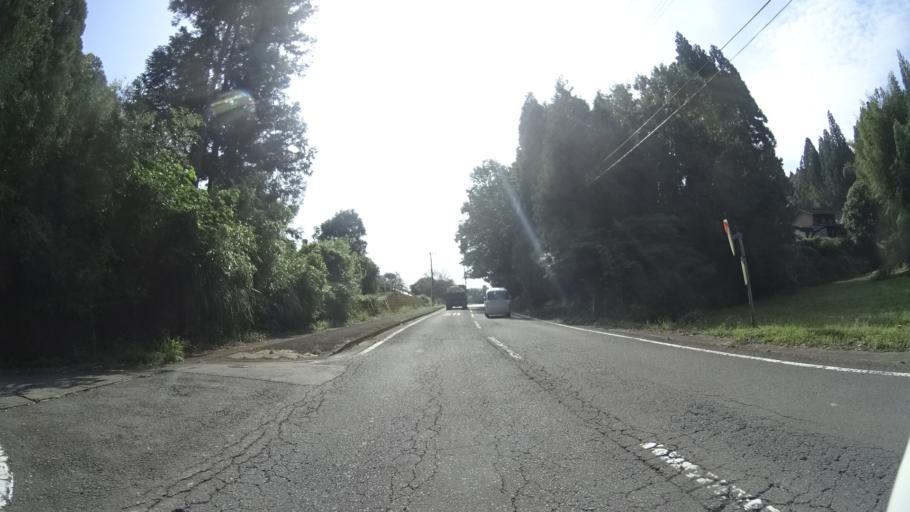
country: JP
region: Miyazaki
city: Kobayashi
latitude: 32.0365
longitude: 130.8210
